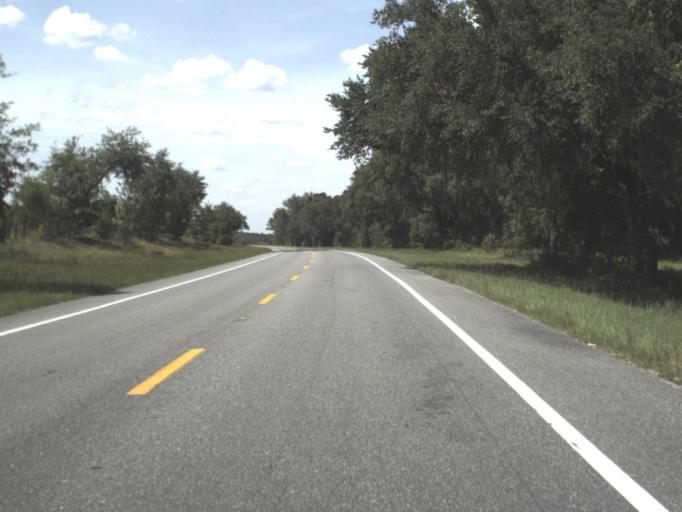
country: US
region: Florida
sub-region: Gilchrist County
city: Trenton
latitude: 29.7388
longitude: -82.7409
